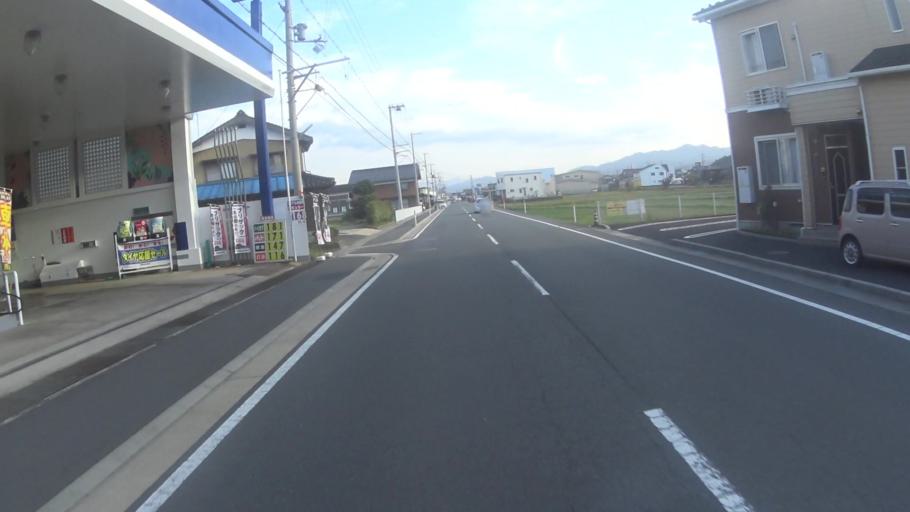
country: JP
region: Kyoto
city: Miyazu
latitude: 35.6246
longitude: 135.0731
